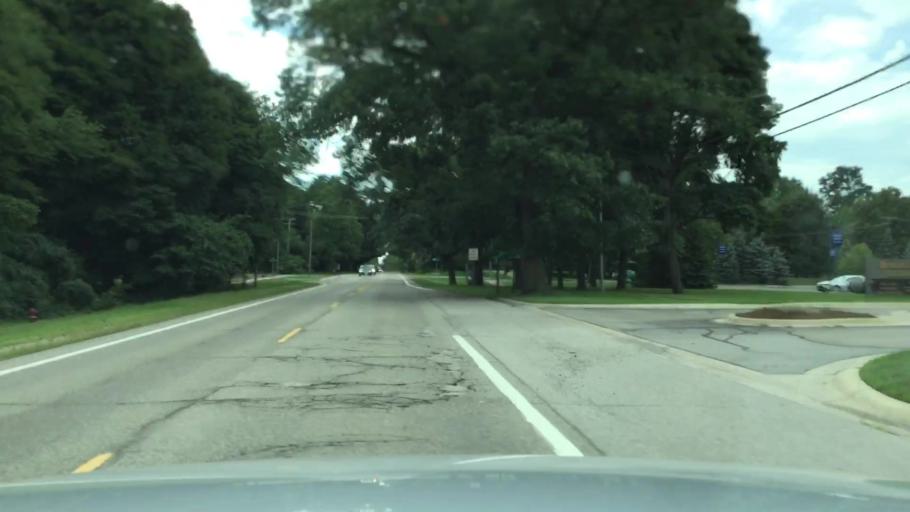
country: US
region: Michigan
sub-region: Oakland County
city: Bloomfield Hills
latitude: 42.5985
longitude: -83.2083
